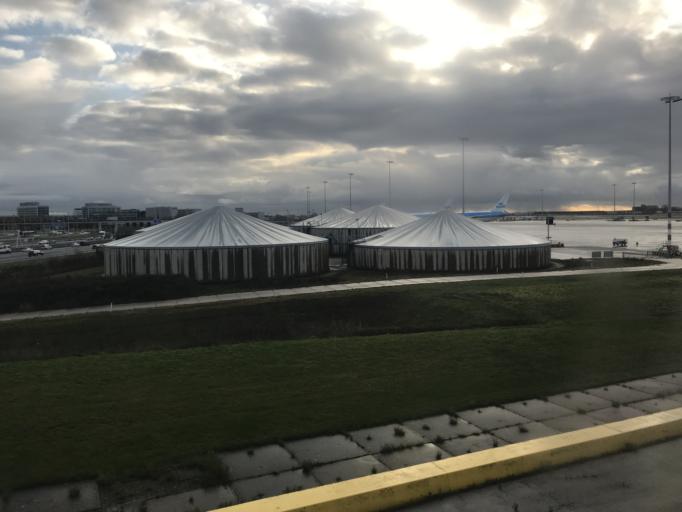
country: NL
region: North Holland
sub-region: Gemeente Aalsmeer
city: Aalsmeer
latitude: 52.3141
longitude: 4.7493
